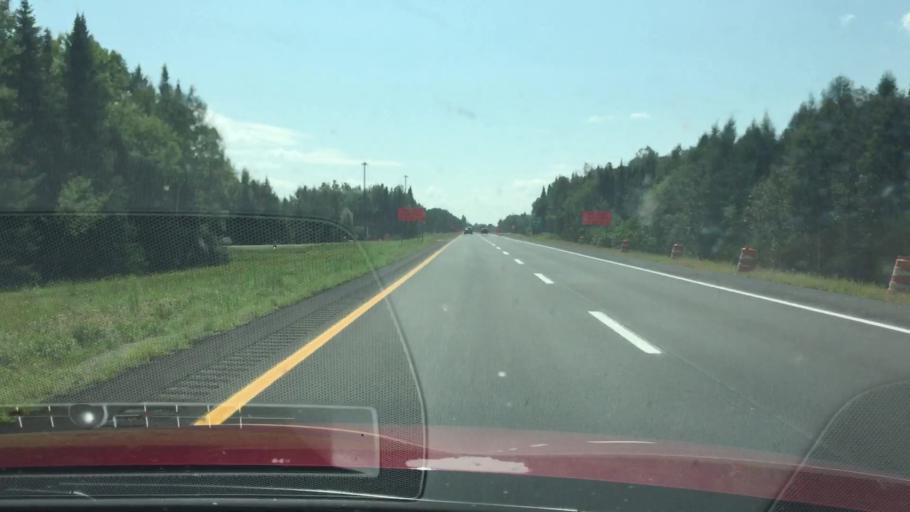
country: US
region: Maine
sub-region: Penobscot County
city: Patten
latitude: 45.8797
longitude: -68.4102
